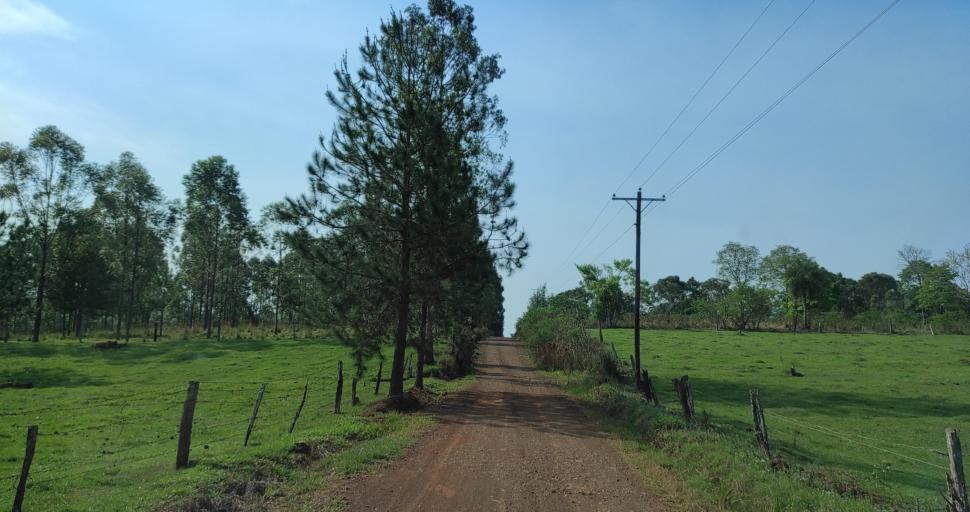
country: AR
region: Misiones
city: Capiovi
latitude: -26.8868
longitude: -55.0486
